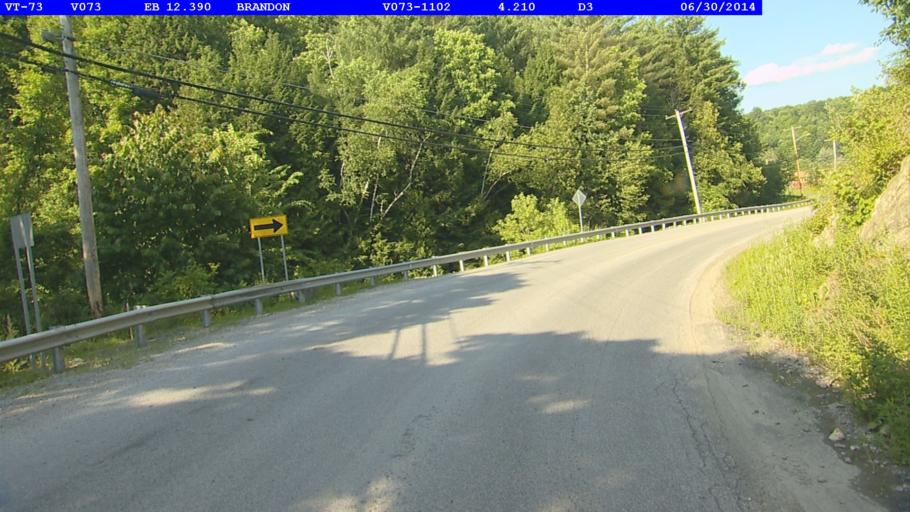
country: US
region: Vermont
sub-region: Rutland County
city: Brandon
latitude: 43.8101
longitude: -73.0759
